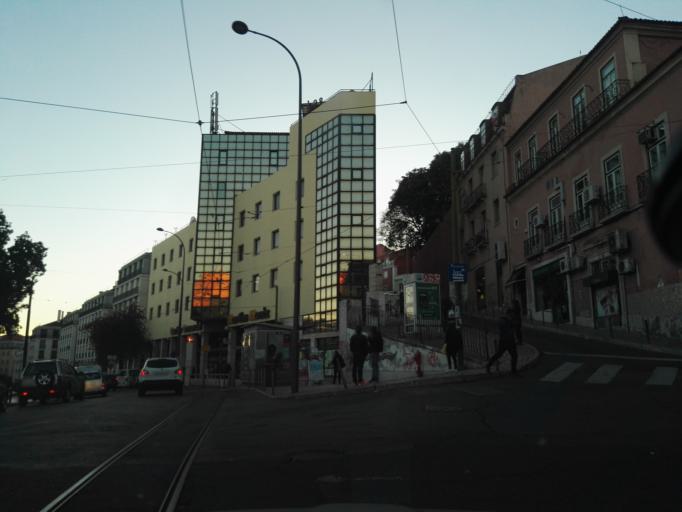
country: PT
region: Lisbon
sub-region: Lisbon
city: Lisbon
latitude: 38.7171
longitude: -9.1361
